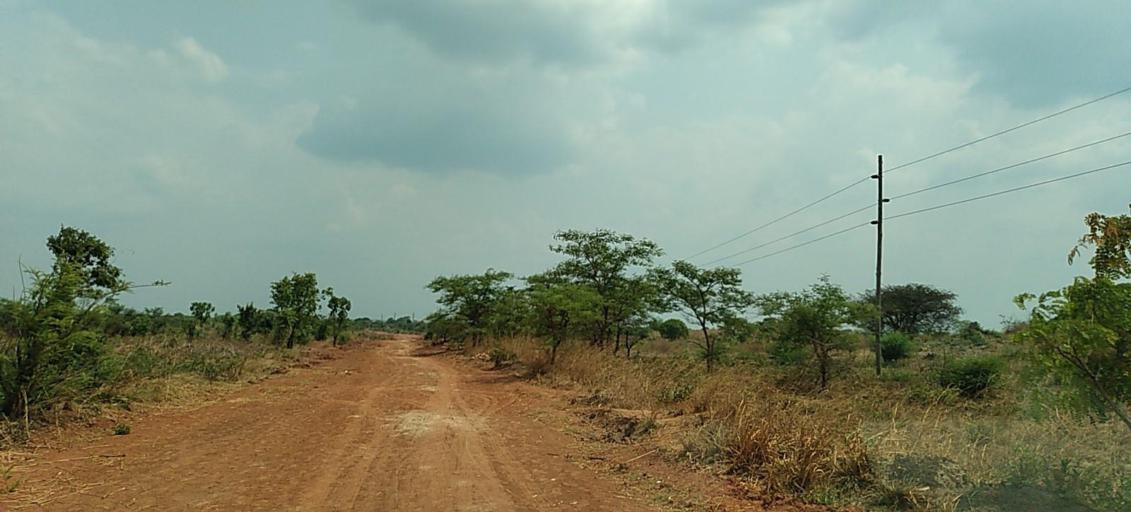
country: ZM
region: Copperbelt
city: Kalulushi
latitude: -12.8843
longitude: 28.0746
